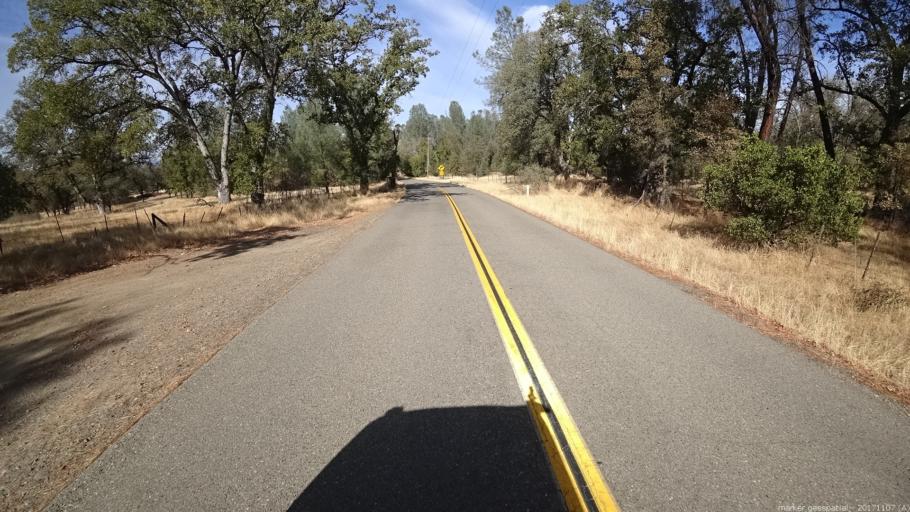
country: US
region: California
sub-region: Shasta County
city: Shasta
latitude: 40.4071
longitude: -122.5201
